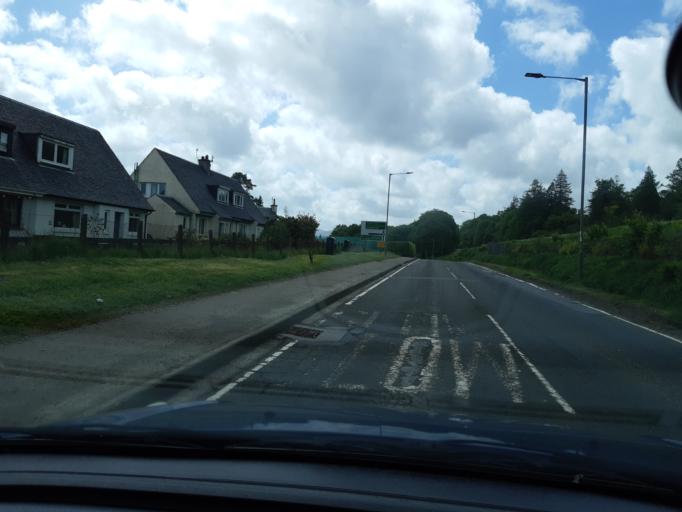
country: GB
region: Scotland
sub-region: Argyll and Bute
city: Lochgilphead
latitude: 56.0392
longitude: -5.4407
